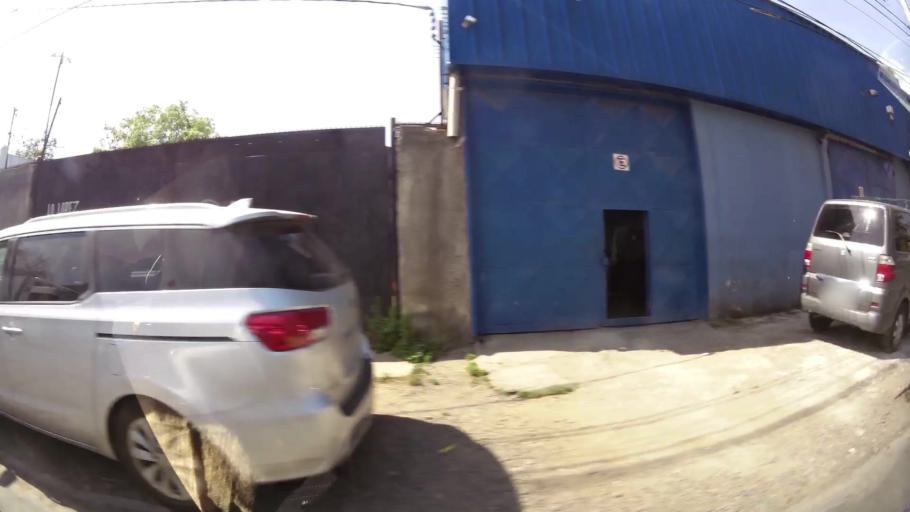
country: CL
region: Santiago Metropolitan
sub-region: Provincia de Santiago
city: Lo Prado
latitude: -33.4267
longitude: -70.7217
